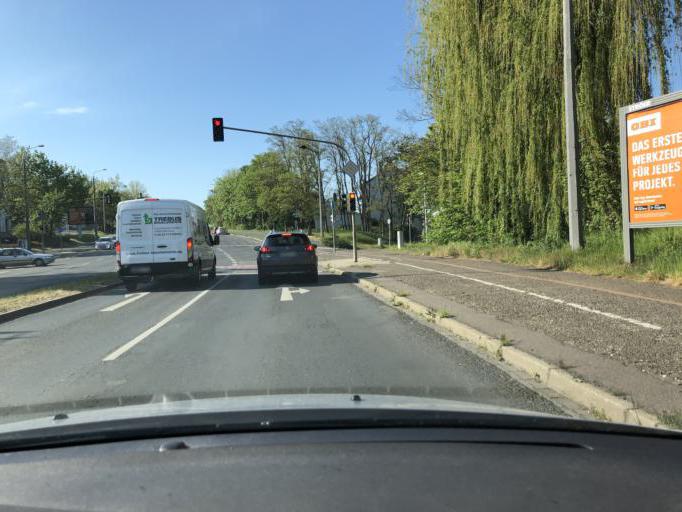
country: DE
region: Thuringia
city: Altenburg
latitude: 50.9974
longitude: 12.4426
